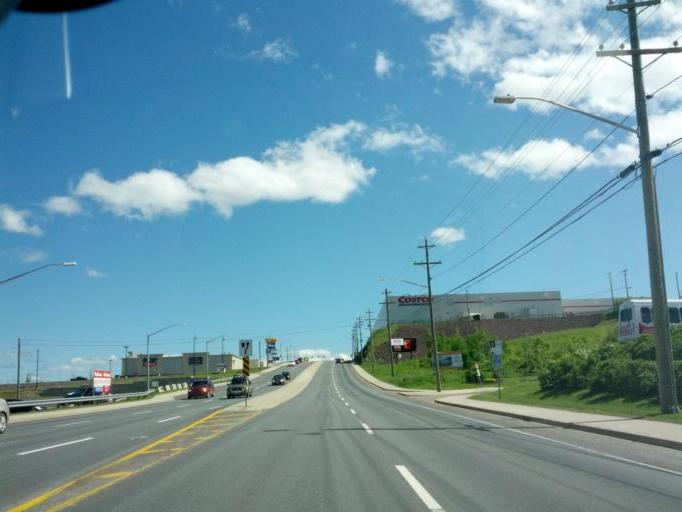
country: CA
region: New Brunswick
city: Moncton
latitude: 46.1209
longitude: -64.8287
